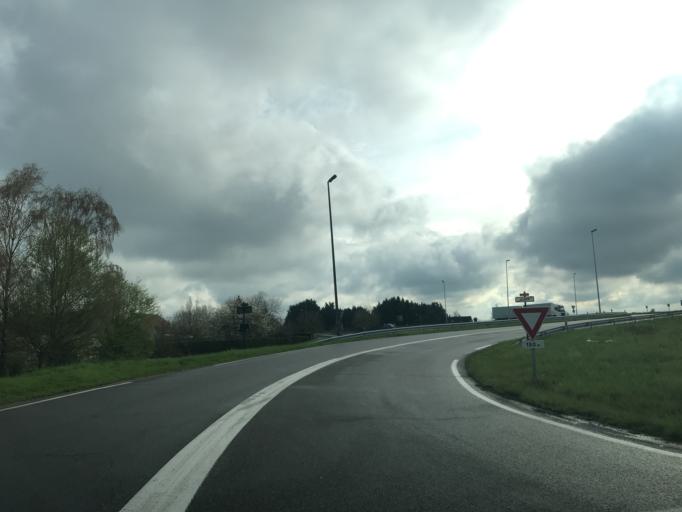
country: FR
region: Centre
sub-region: Departement du Loiret
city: Gien
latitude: 47.6869
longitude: 2.6522
